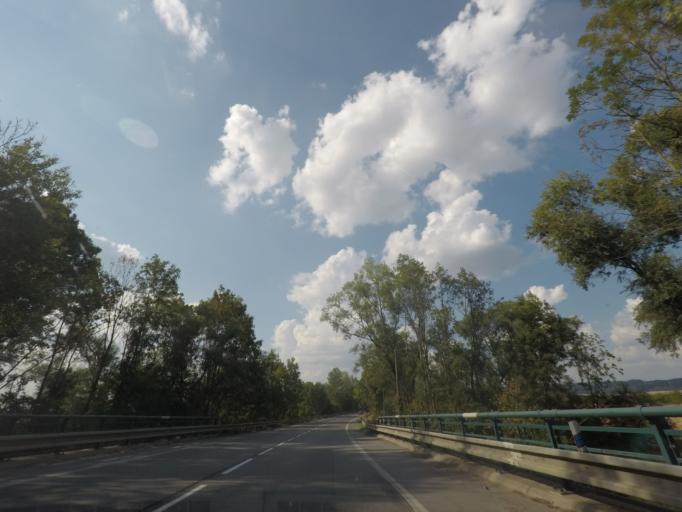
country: CZ
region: Kralovehradecky
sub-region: Okres Nachod
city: Jaromer
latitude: 50.4074
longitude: 15.8861
